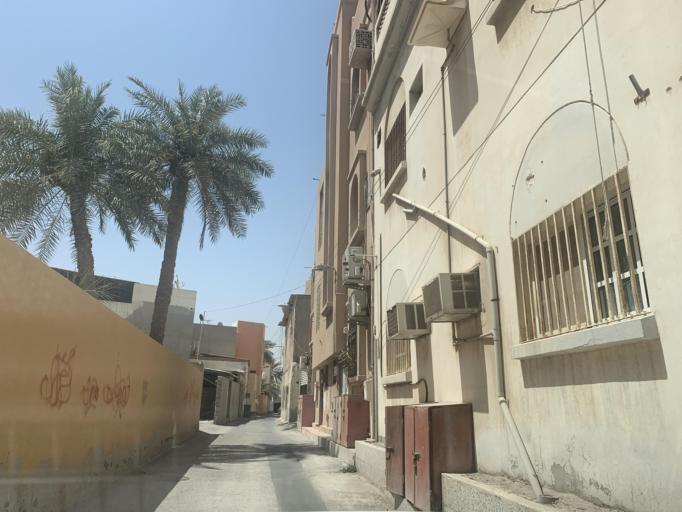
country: BH
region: Manama
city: Jidd Hafs
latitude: 26.2184
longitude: 50.5334
